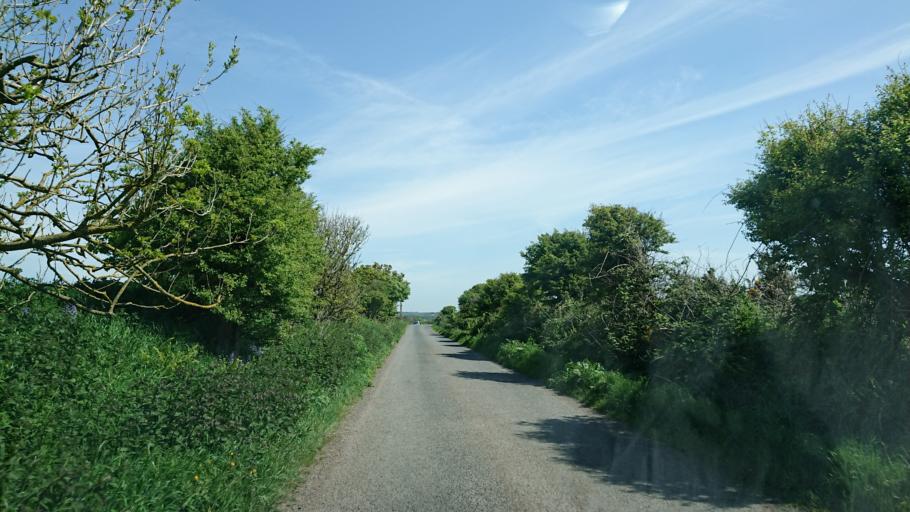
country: IE
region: Munster
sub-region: Waterford
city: Tra Mhor
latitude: 52.1464
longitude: -7.0815
